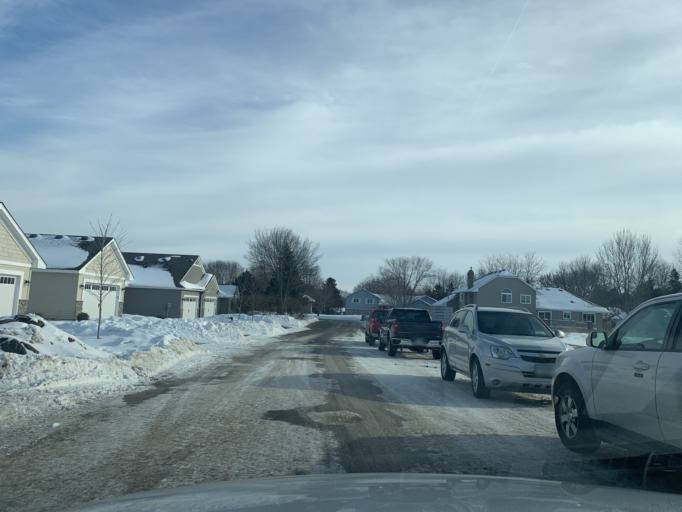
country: US
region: Minnesota
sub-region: Wright County
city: Saint Michael
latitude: 45.2078
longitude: -93.6566
